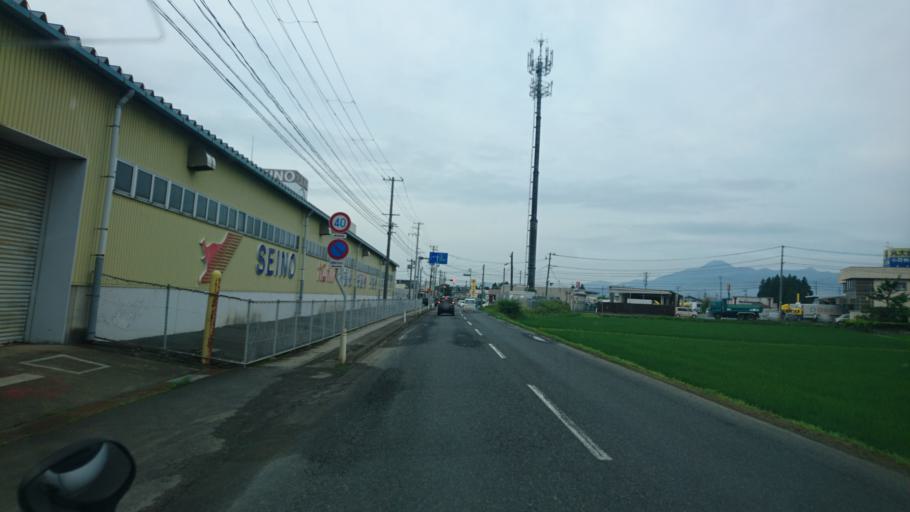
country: JP
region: Iwate
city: Morioka-shi
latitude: 39.6589
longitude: 141.1413
